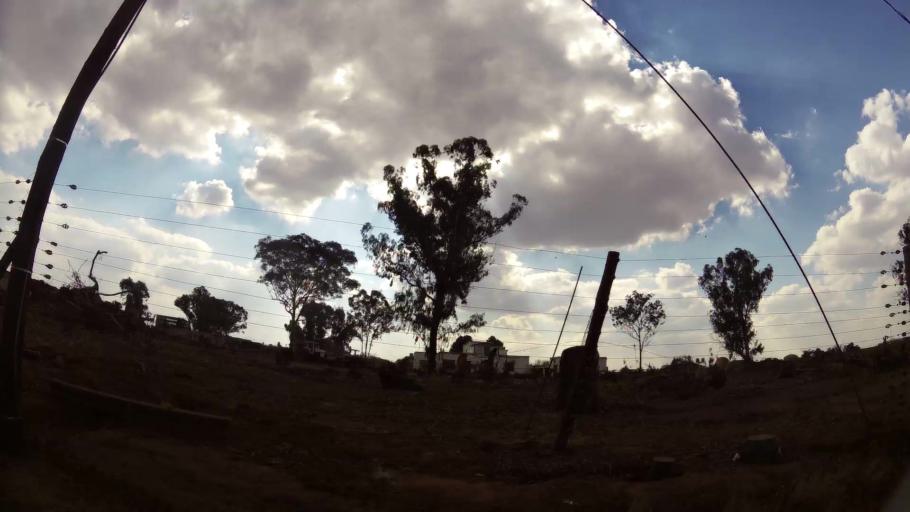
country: ZA
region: Mpumalanga
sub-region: Nkangala District Municipality
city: Delmas
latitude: -26.1315
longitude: 28.6710
